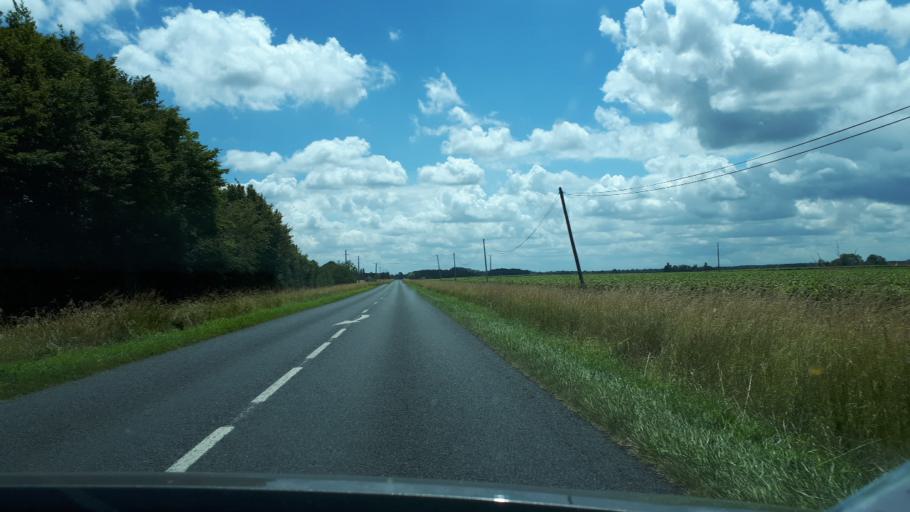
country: FR
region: Centre
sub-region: Departement du Loir-et-Cher
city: Contres
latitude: 47.3843
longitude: 1.4075
